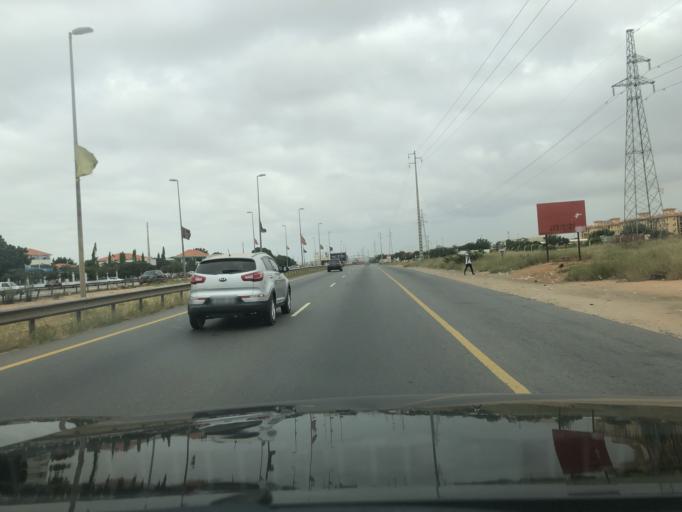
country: AO
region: Luanda
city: Luanda
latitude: -8.9733
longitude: 13.2390
